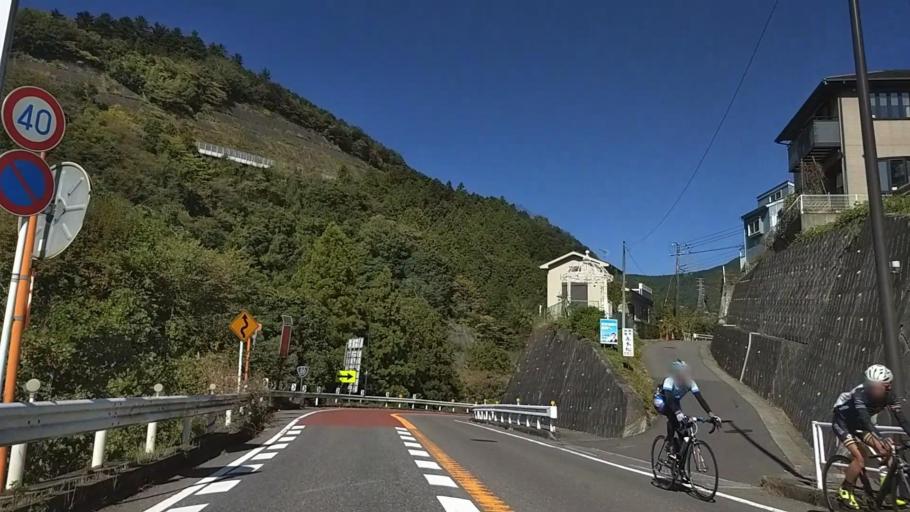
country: JP
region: Yamanashi
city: Uenohara
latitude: 35.6238
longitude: 139.2034
